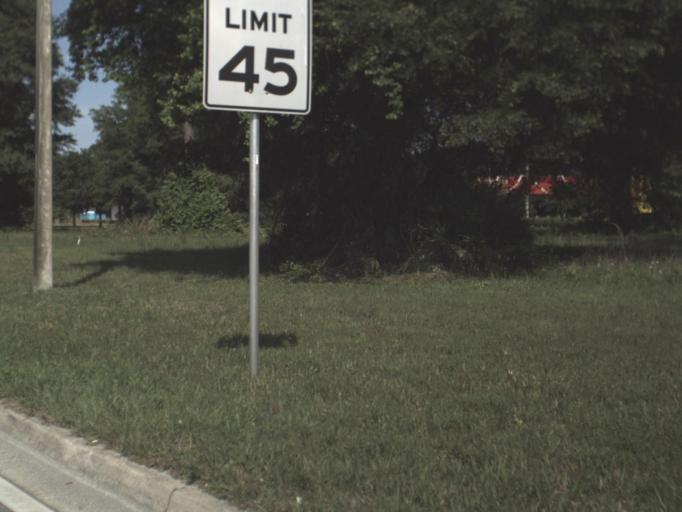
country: US
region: Florida
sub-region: Duval County
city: Jacksonville
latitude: 30.2451
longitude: -81.5987
